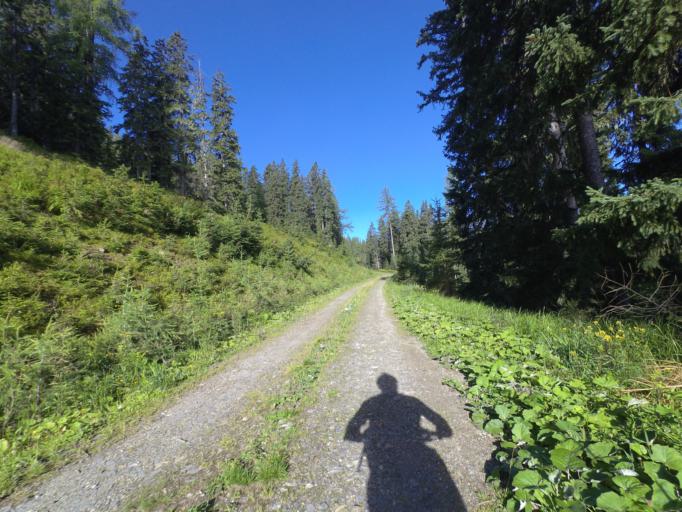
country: AT
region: Salzburg
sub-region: Politischer Bezirk Sankt Johann im Pongau
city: Goldegg
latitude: 47.3531
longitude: 13.0829
